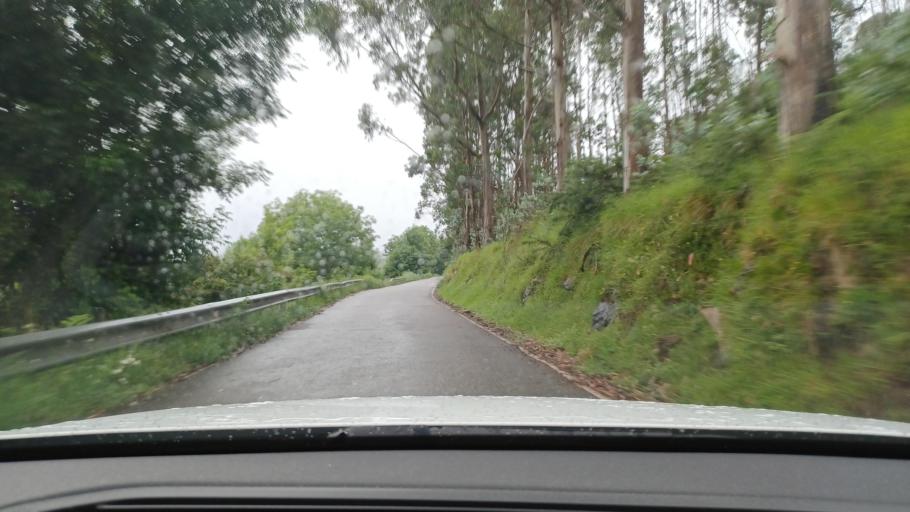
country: ES
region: Asturias
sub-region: Province of Asturias
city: Castandiello
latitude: 43.3001
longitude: -5.9422
